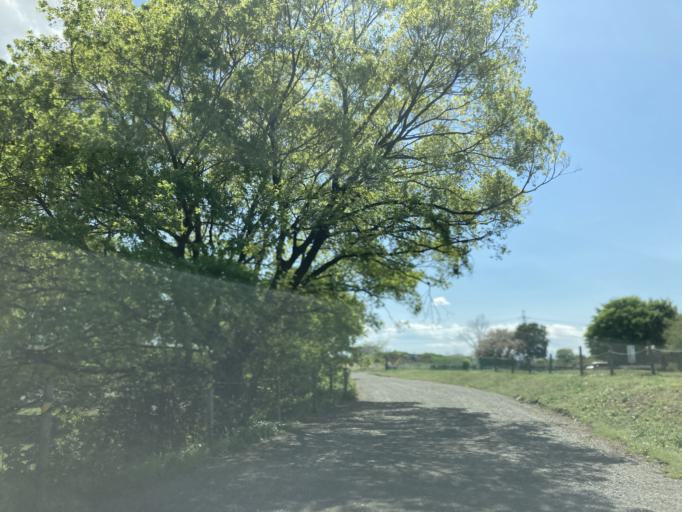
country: JP
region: Saitama
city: Sayama
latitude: 35.8841
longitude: 139.4144
